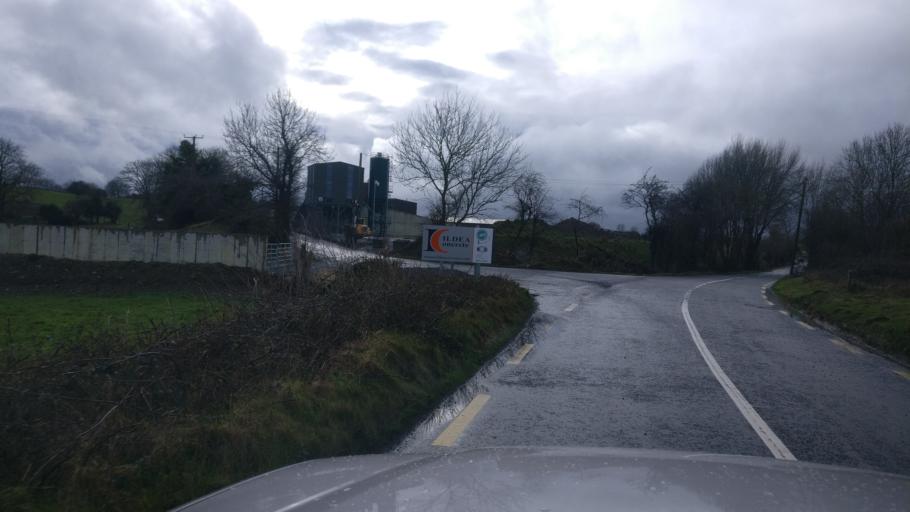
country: IE
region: Leinster
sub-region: An Iarmhi
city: Athlone
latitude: 53.4239
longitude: -8.0349
